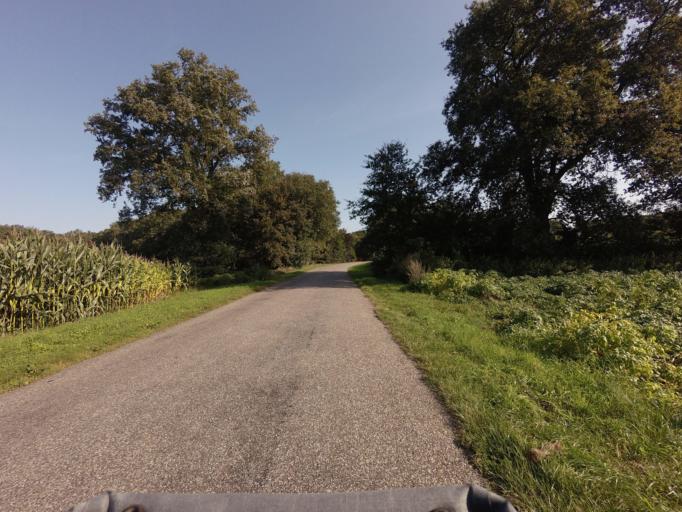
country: DE
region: Lower Saxony
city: Wielen
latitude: 52.5490
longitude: 6.7352
